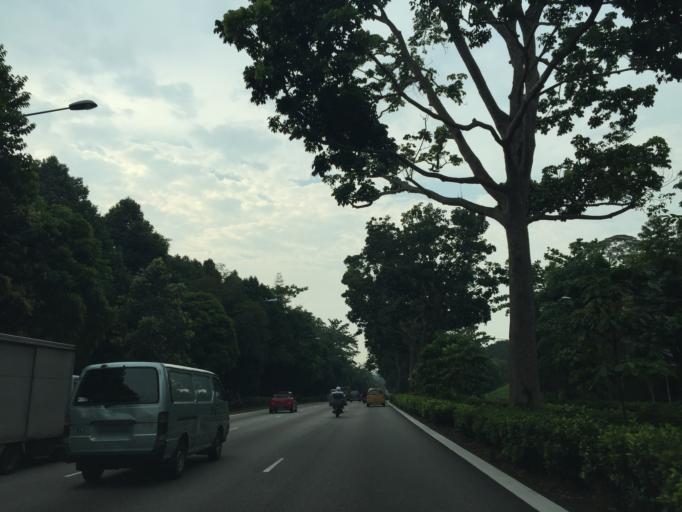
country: MY
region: Johor
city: Johor Bahru
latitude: 1.3817
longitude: 103.7755
